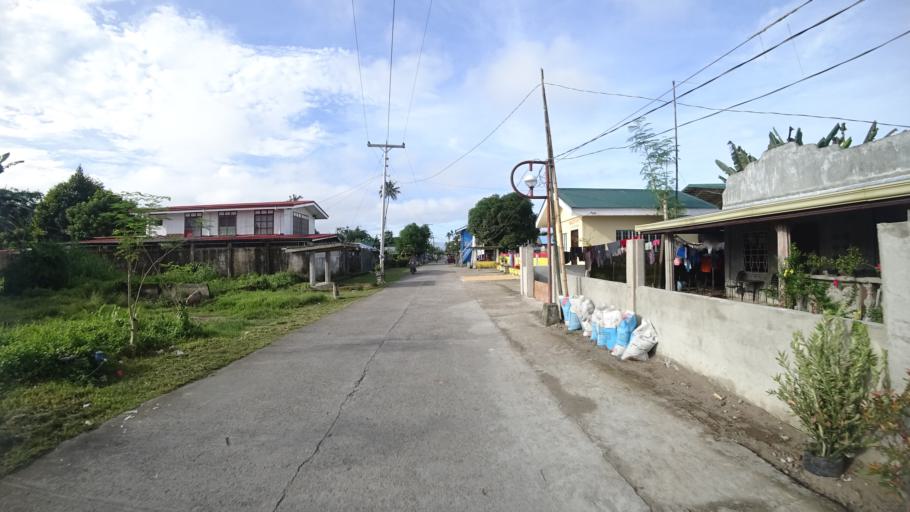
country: PH
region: Eastern Visayas
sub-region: Province of Leyte
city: Alangalang
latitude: 11.1808
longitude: 124.8716
